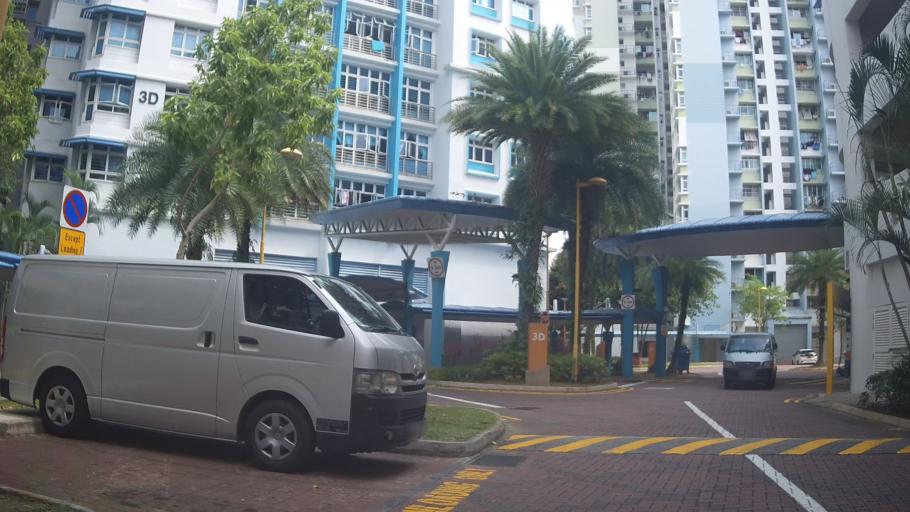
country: SG
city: Singapore
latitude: 1.3131
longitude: 103.8723
